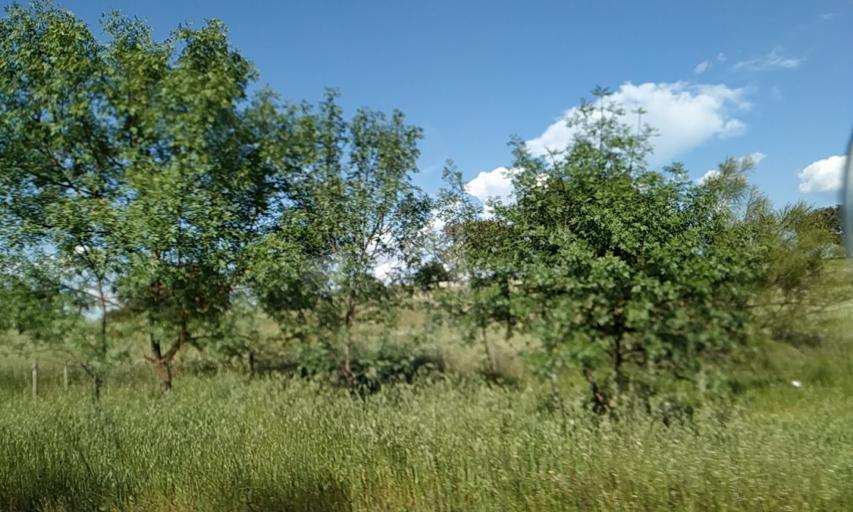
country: PT
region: Portalegre
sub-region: Fronteira
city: Fronteira
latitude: 39.0084
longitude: -7.4674
